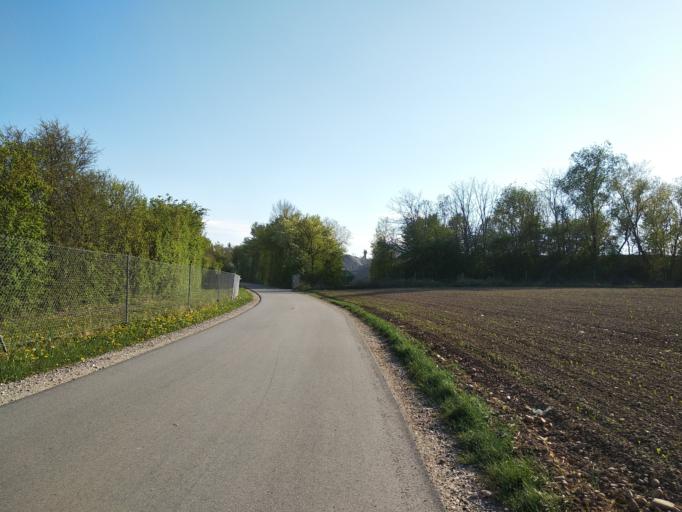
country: DE
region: Bavaria
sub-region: Upper Bavaria
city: Grasbrunn
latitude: 48.0739
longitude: 11.7365
